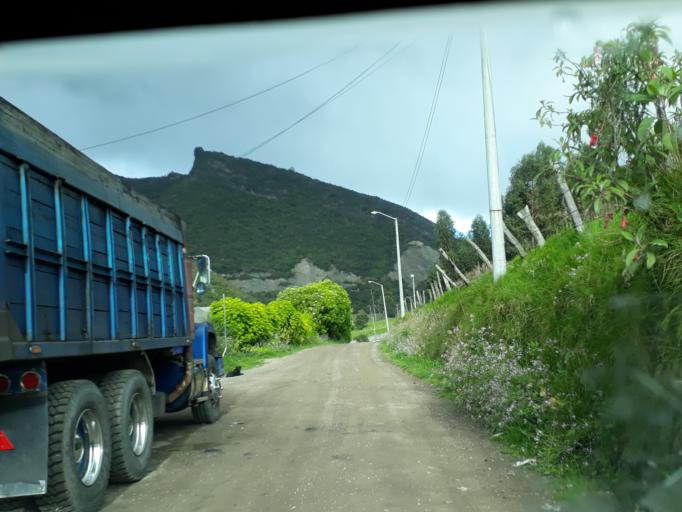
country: CO
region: Cundinamarca
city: Sutatausa
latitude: 5.1942
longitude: -73.8890
